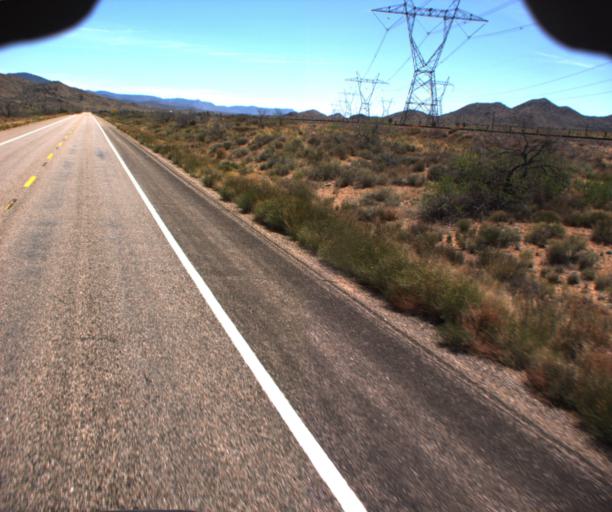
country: US
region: Arizona
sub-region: Mohave County
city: New Kingman-Butler
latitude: 35.3960
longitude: -113.7518
